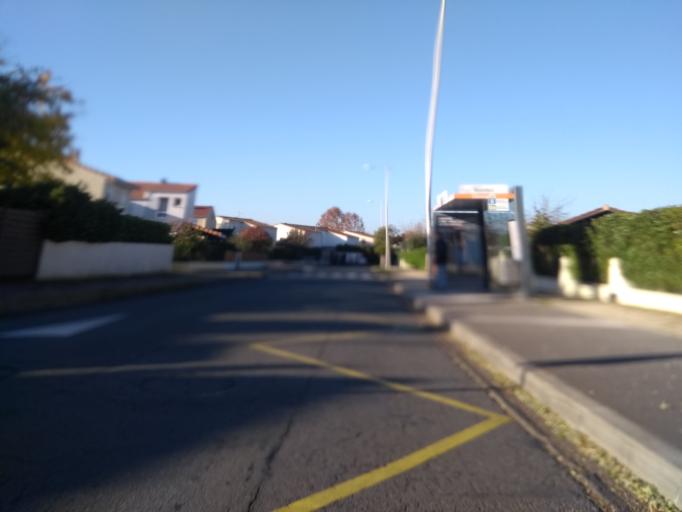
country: FR
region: Aquitaine
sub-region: Departement de la Gironde
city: Gradignan
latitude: 44.7691
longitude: -0.5956
